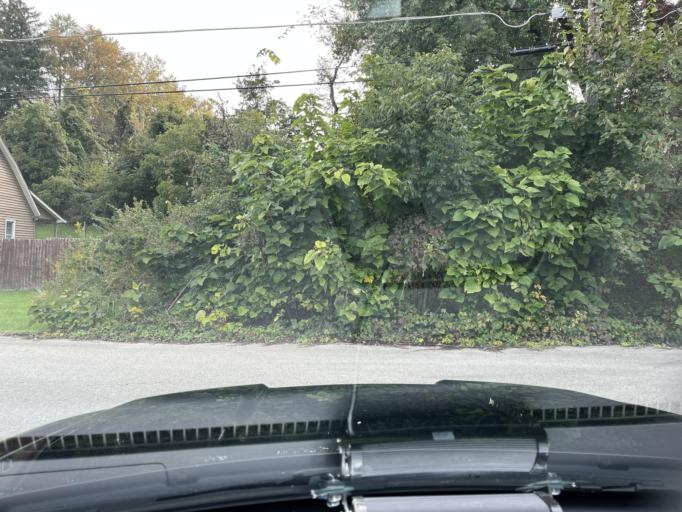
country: US
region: Pennsylvania
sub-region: Fayette County
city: Leith-Hatfield
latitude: 39.8891
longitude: -79.7272
